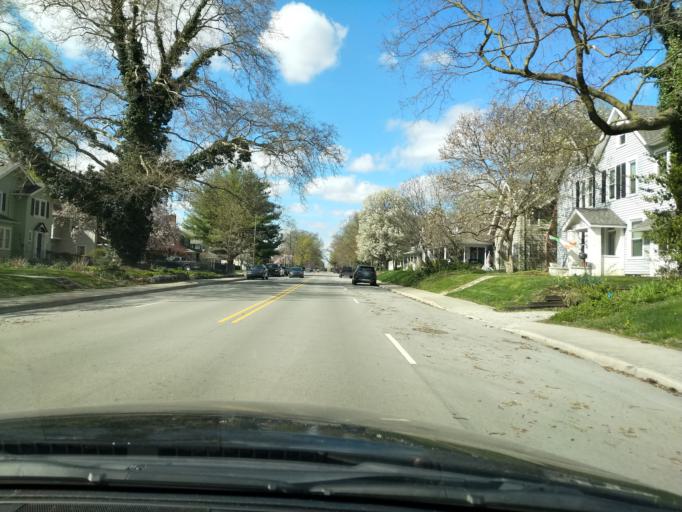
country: US
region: Indiana
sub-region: Marion County
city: Broad Ripple
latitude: 39.8438
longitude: -86.1500
